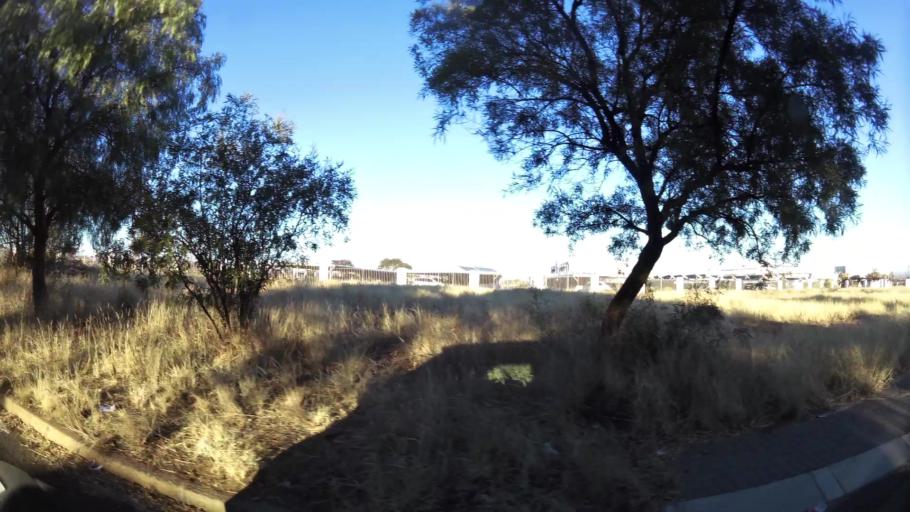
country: ZA
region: Northern Cape
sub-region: Frances Baard District Municipality
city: Kimberley
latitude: -28.7641
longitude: 24.7388
